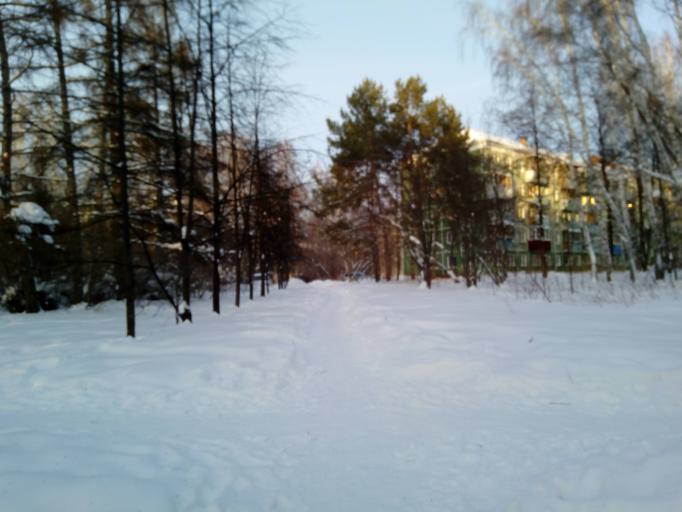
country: RU
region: Novosibirsk
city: Akademgorodok
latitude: 54.8378
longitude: 83.1098
